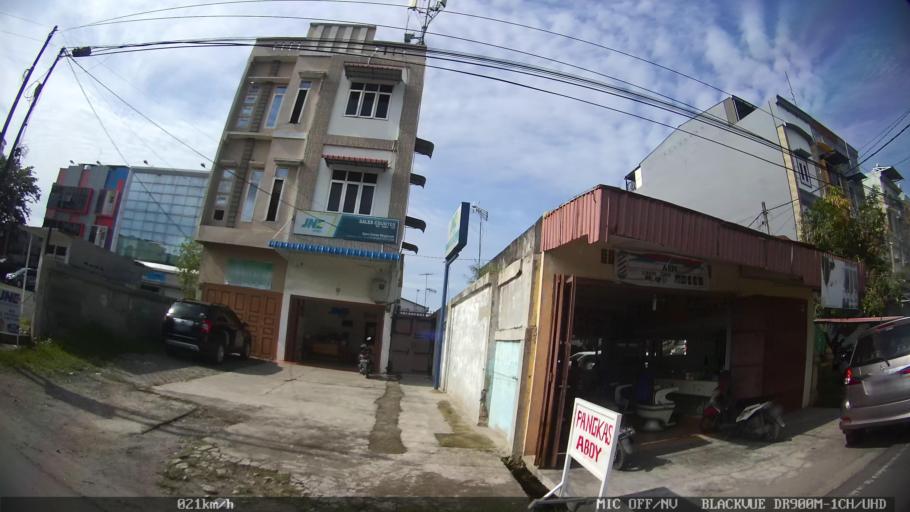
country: ID
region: North Sumatra
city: Medan
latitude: 3.6045
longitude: 98.6504
